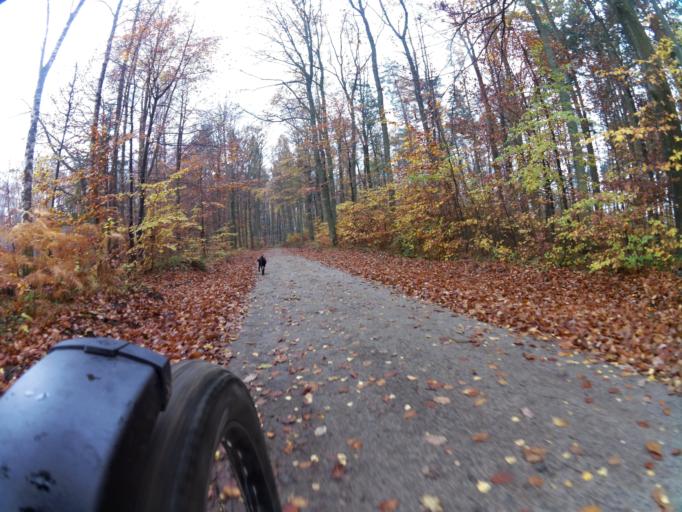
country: PL
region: Pomeranian Voivodeship
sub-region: Powiat pucki
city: Krokowa
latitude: 54.7675
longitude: 18.0951
